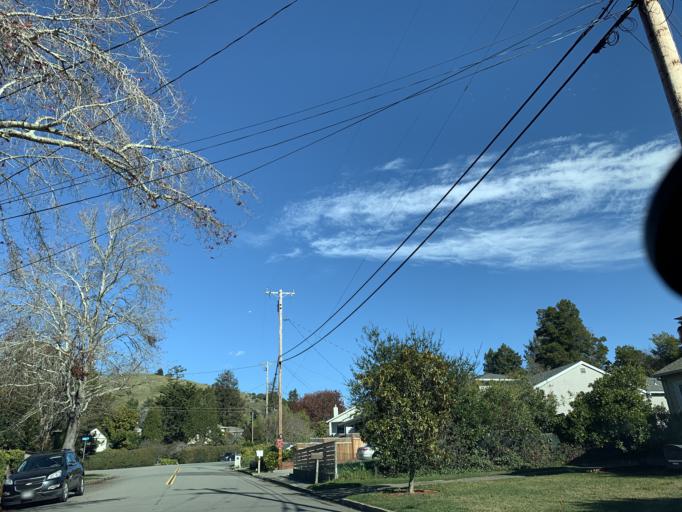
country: US
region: California
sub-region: Marin County
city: Strawberry
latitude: 37.9058
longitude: -122.5174
